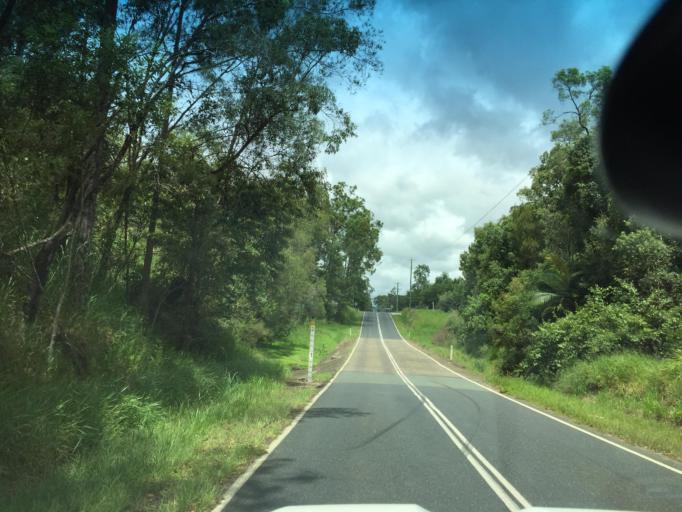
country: AU
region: Queensland
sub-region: Moreton Bay
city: Caboolture
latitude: -27.0501
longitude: 152.9119
